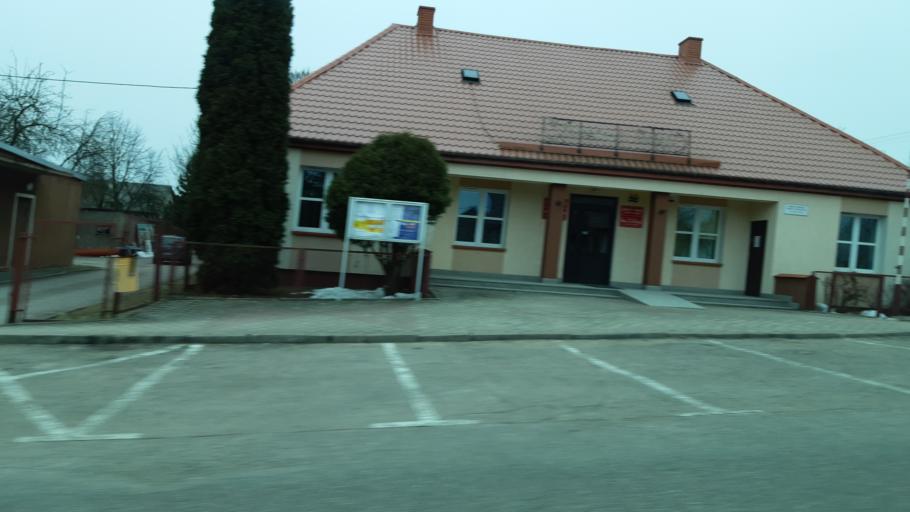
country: PL
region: Podlasie
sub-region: Suwalki
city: Suwalki
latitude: 54.3266
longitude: 22.9664
